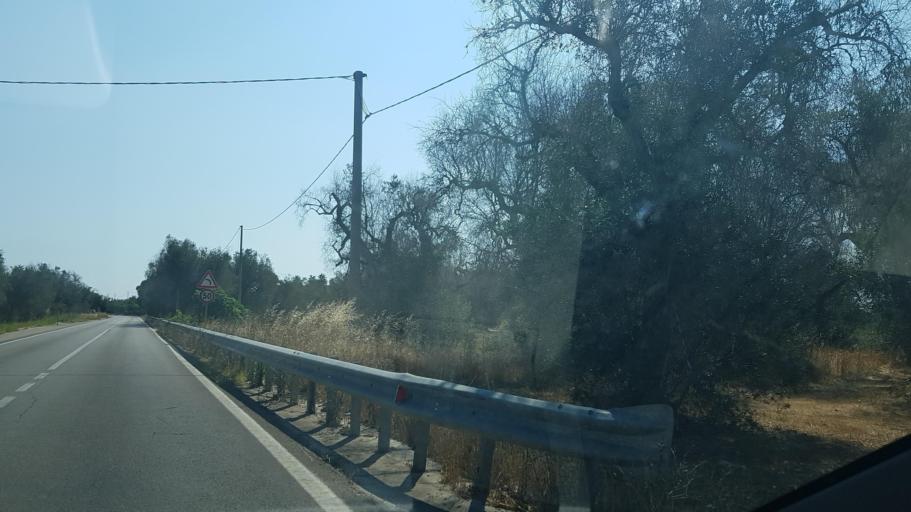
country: IT
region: Apulia
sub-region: Provincia di Lecce
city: Ruffano
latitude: 39.9980
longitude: 18.2674
